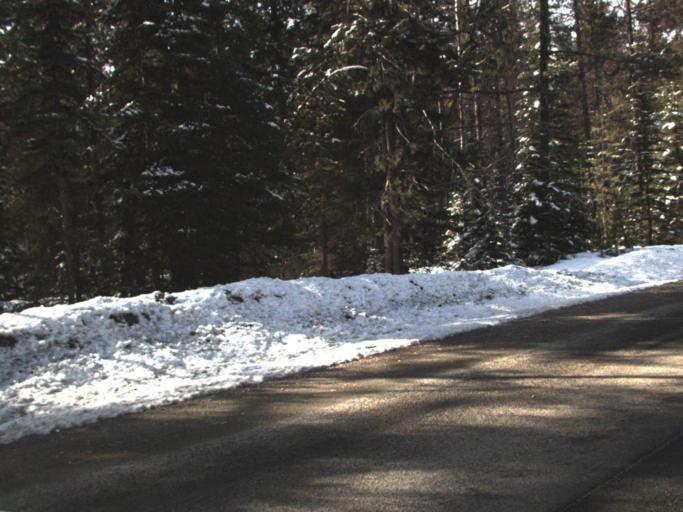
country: US
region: Washington
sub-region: Stevens County
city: Colville
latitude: 48.6520
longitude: -117.4880
